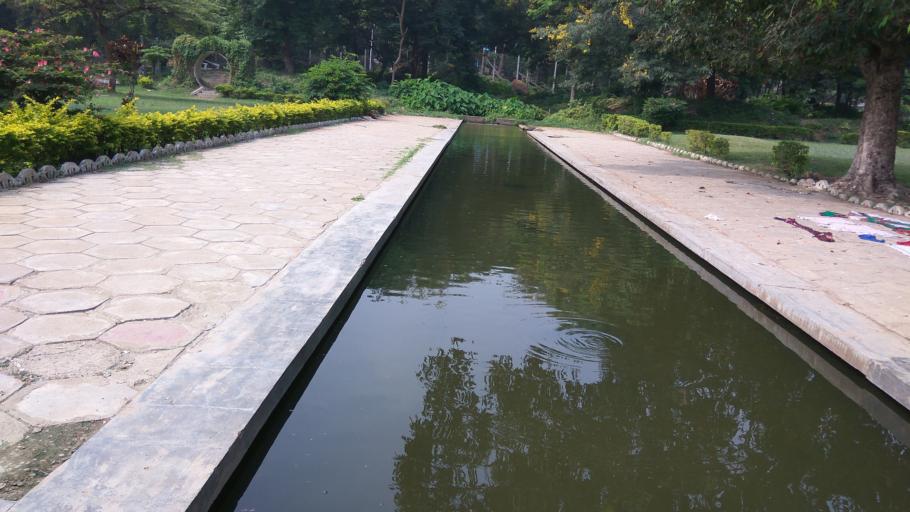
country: IN
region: Tamil Nadu
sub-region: Krishnagiri
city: Krishnagiri
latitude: 12.4740
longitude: 78.1852
